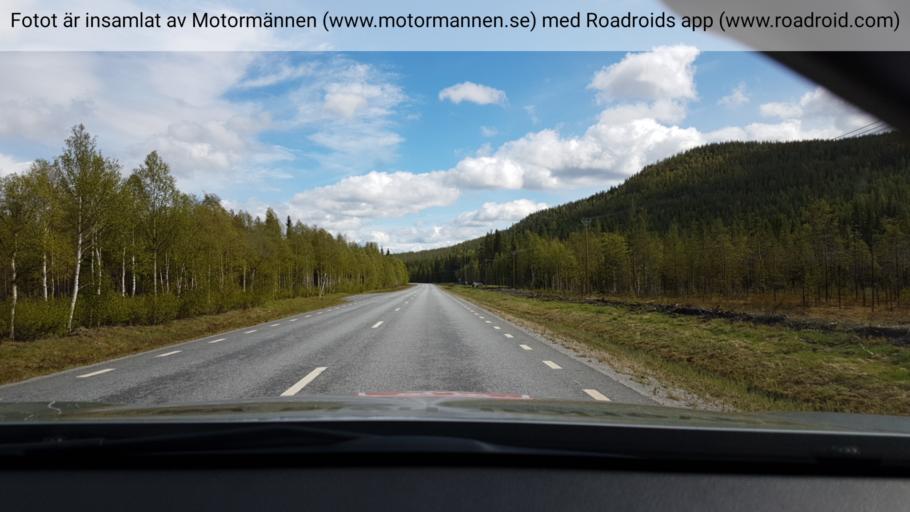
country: SE
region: Vaesterbotten
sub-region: Asele Kommun
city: Insjon
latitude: 64.1723
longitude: 17.7989
